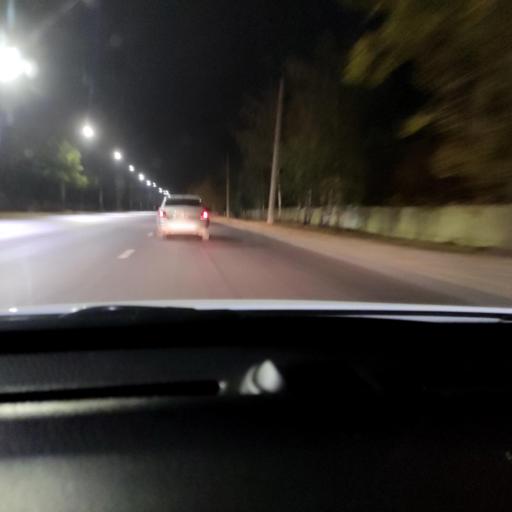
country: RU
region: Voronezj
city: Somovo
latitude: 51.7088
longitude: 39.2767
